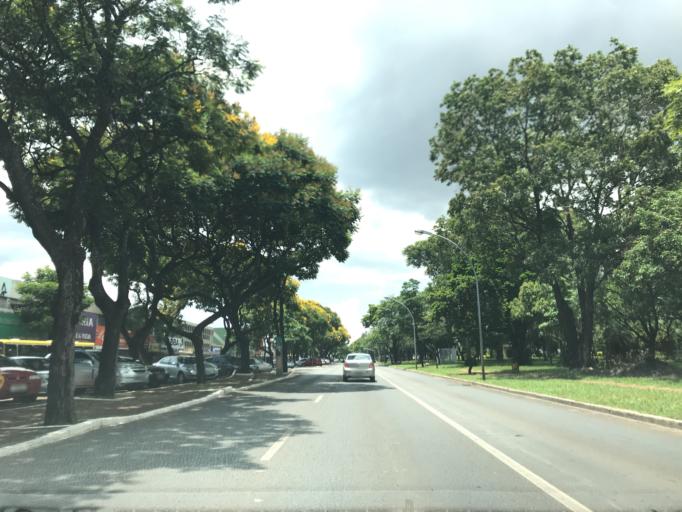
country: BR
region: Federal District
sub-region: Brasilia
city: Brasilia
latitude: -15.8239
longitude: -47.9223
